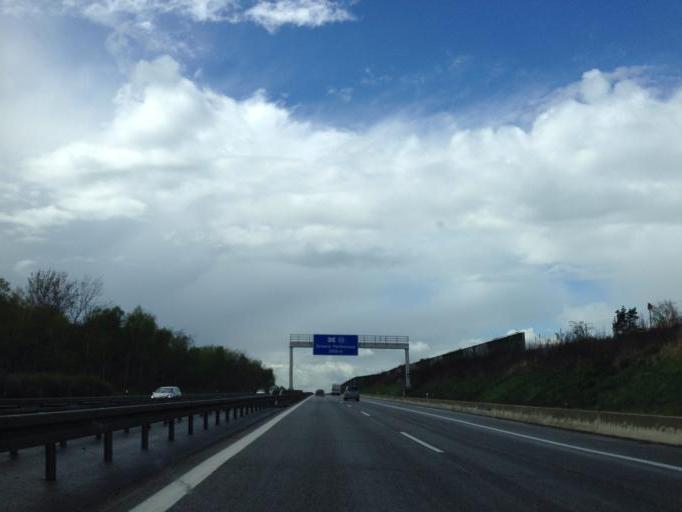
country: DE
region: Saxony
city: Naunhof
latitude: 51.3073
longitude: 12.5866
